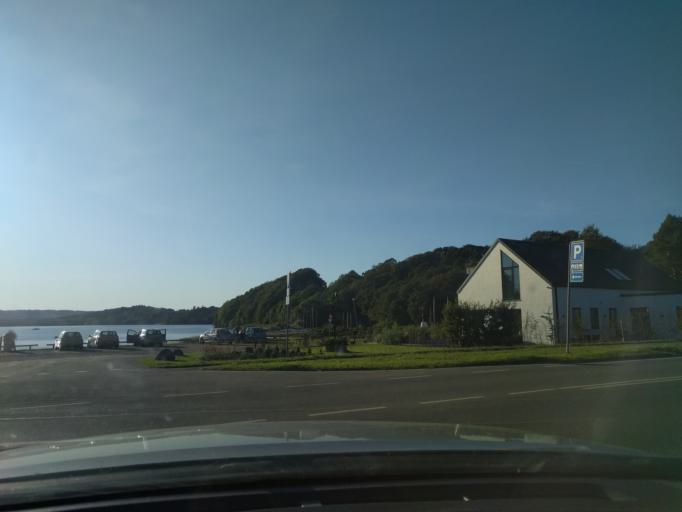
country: DK
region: Central Jutland
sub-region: Skanderborg Kommune
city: Ry
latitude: 56.1042
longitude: 9.7847
